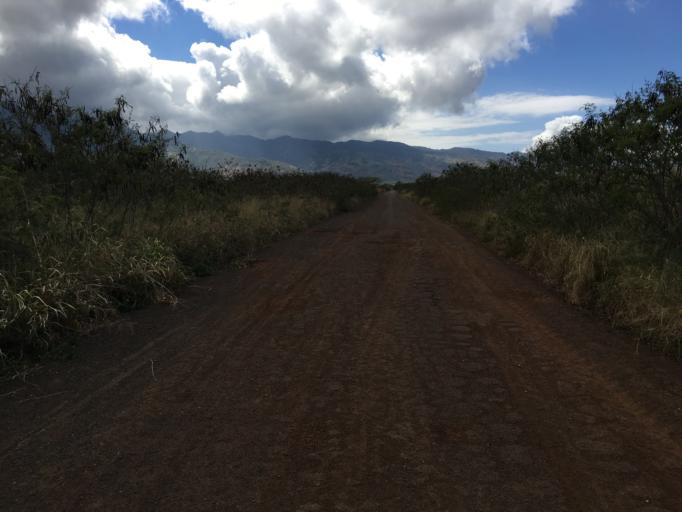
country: US
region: Hawaii
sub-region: Honolulu County
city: Hale'iwa
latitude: 21.5828
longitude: -158.1165
